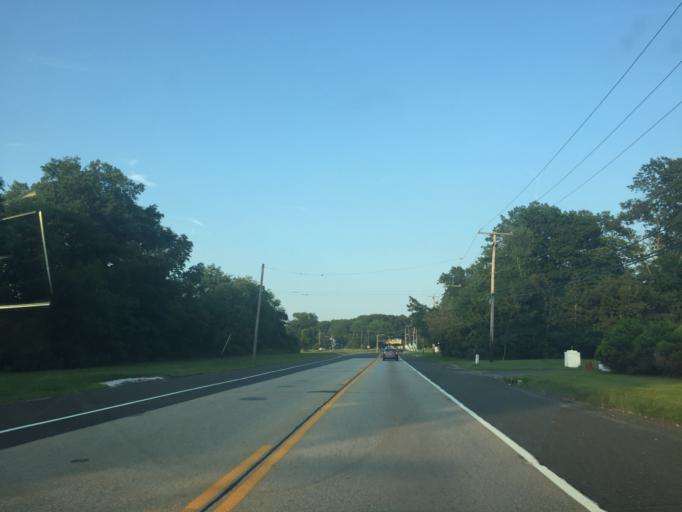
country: US
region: New Jersey
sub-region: Monmouth County
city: Shark River Hills
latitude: 40.2292
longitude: -74.0645
